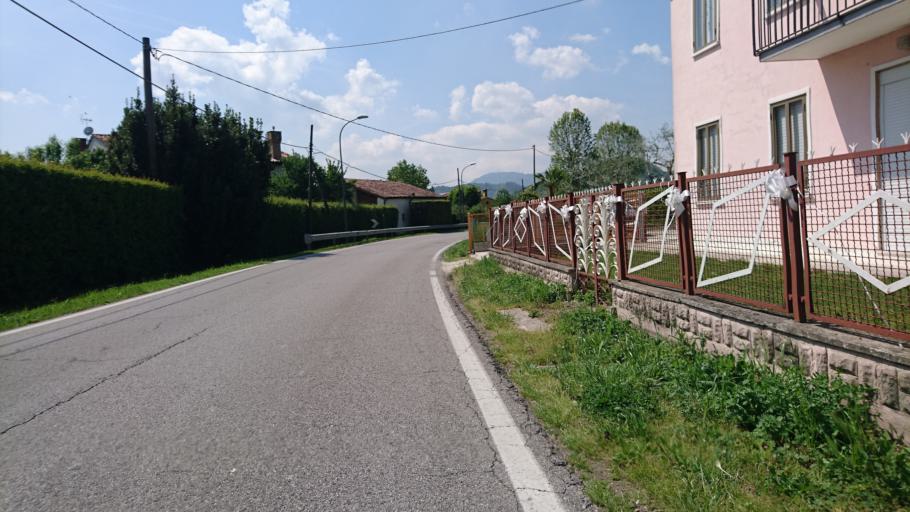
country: IT
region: Veneto
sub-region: Provincia di Padova
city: San Biagio
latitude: 45.3657
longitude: 11.7508
